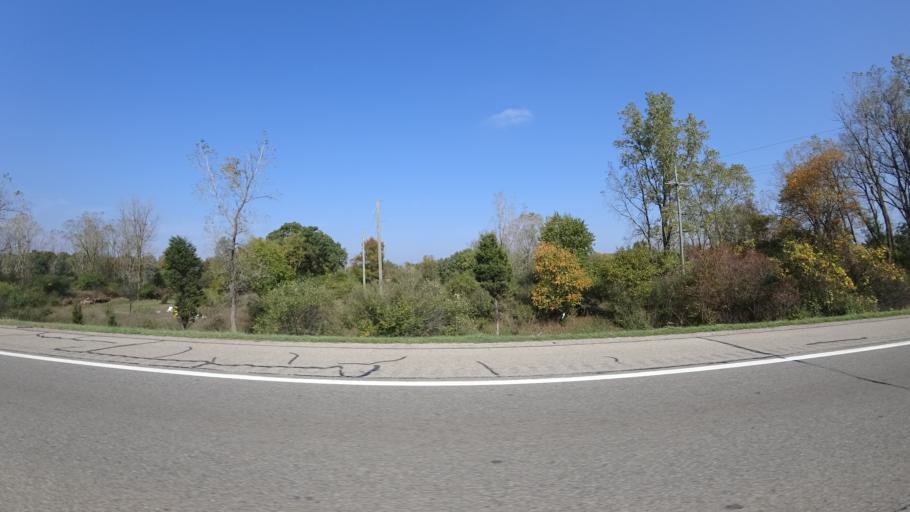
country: US
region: Michigan
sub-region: Washtenaw County
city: Dexter
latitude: 42.2984
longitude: -83.8576
